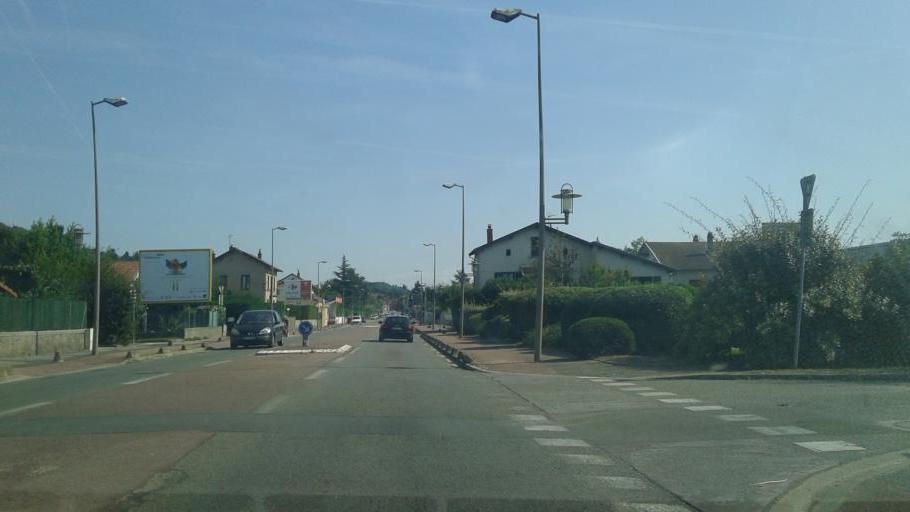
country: FR
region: Rhone-Alpes
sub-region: Departement de l'Ain
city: La Boisse
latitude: 45.8466
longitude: 5.0417
